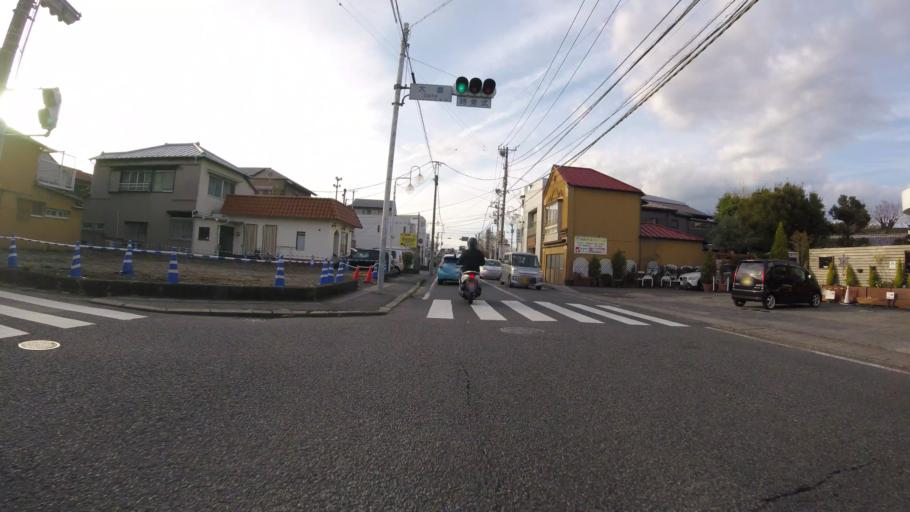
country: JP
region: Shizuoka
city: Mishima
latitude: 35.0919
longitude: 138.9366
